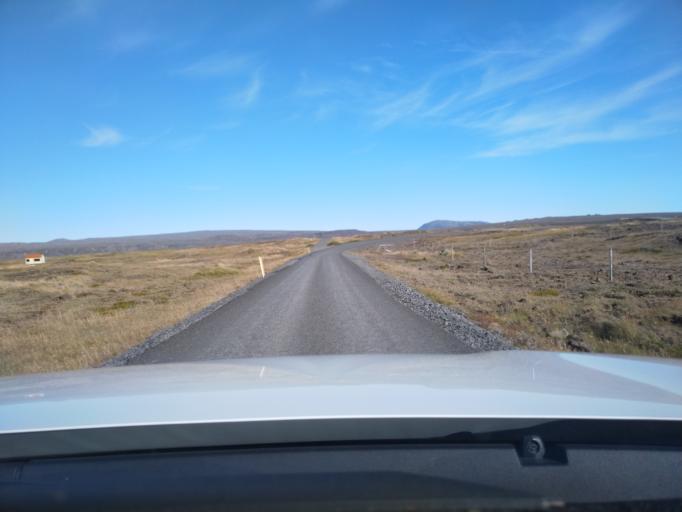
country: IS
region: South
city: THorlakshoefn
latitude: 63.8327
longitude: -21.6740
